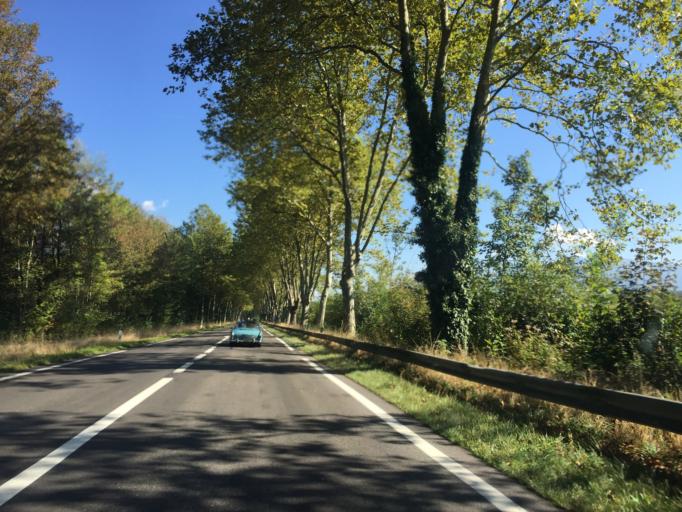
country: FR
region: Rhone-Alpes
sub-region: Departement de la Savoie
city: Coise-Saint-Jean-Pied-Gauthier
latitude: 45.5422
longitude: 6.1380
